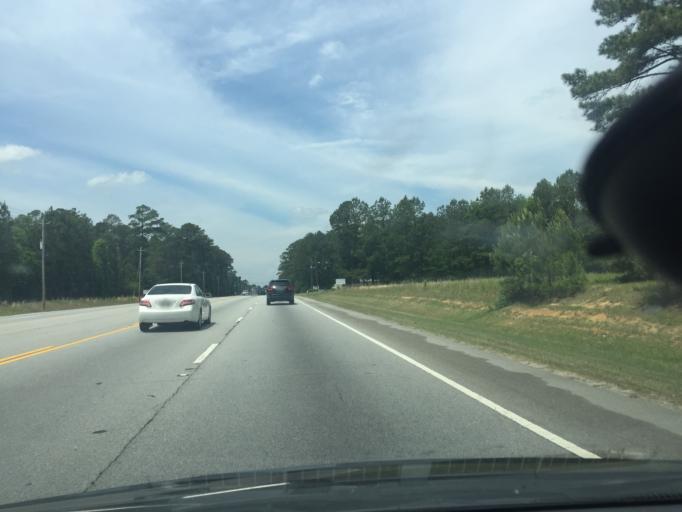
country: US
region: Georgia
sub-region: Chatham County
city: Bloomingdale
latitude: 32.1394
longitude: -81.3207
